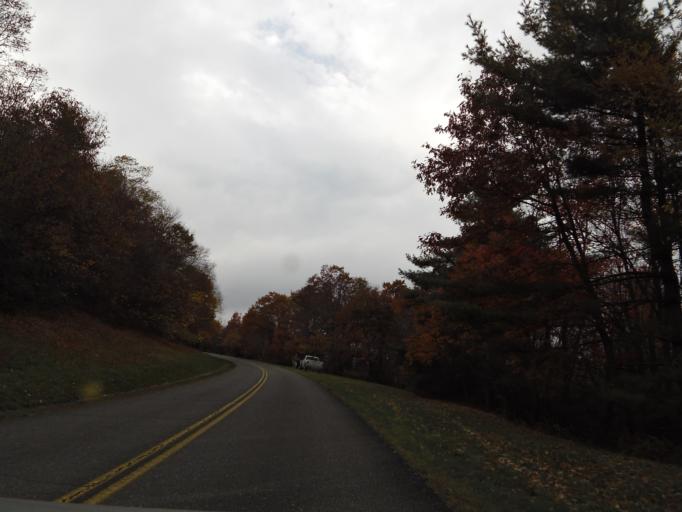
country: US
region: North Carolina
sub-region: Ashe County
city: West Jefferson
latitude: 36.2943
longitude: -81.4089
